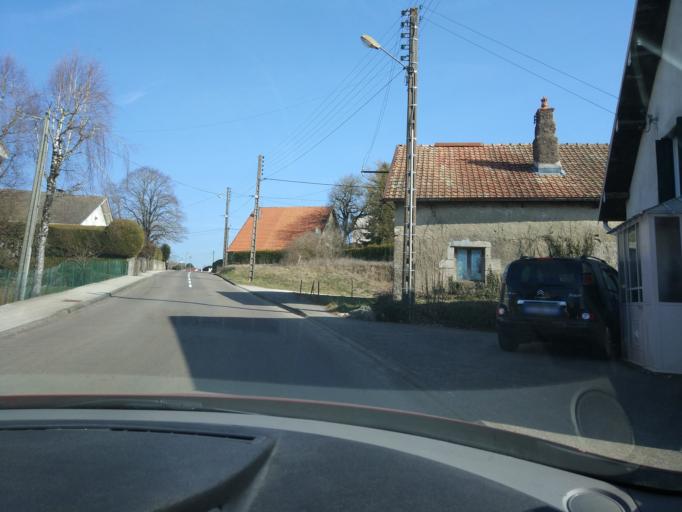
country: FR
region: Franche-Comte
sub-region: Departement du Doubs
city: Saone
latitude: 47.2252
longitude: 6.1187
